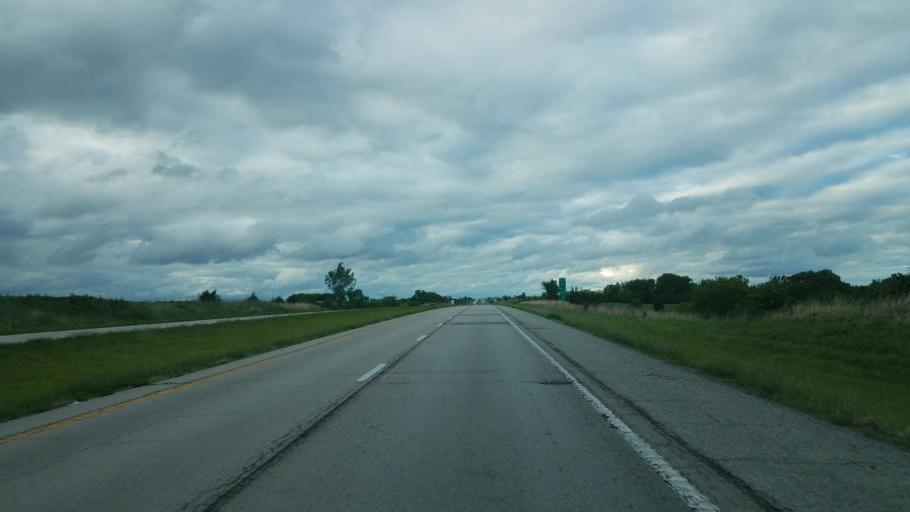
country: US
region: Iowa
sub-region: Decatur County
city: Lamoni
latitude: 40.4901
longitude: -93.9702
